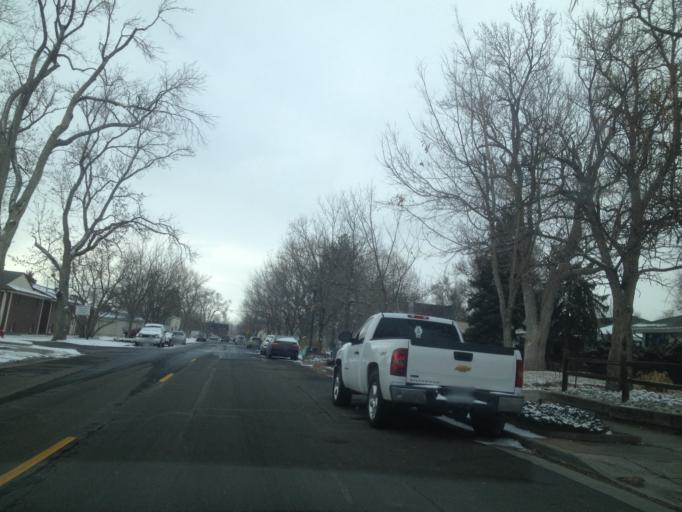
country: US
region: Colorado
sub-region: Adams County
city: Westminster
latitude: 39.8291
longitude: -105.0369
